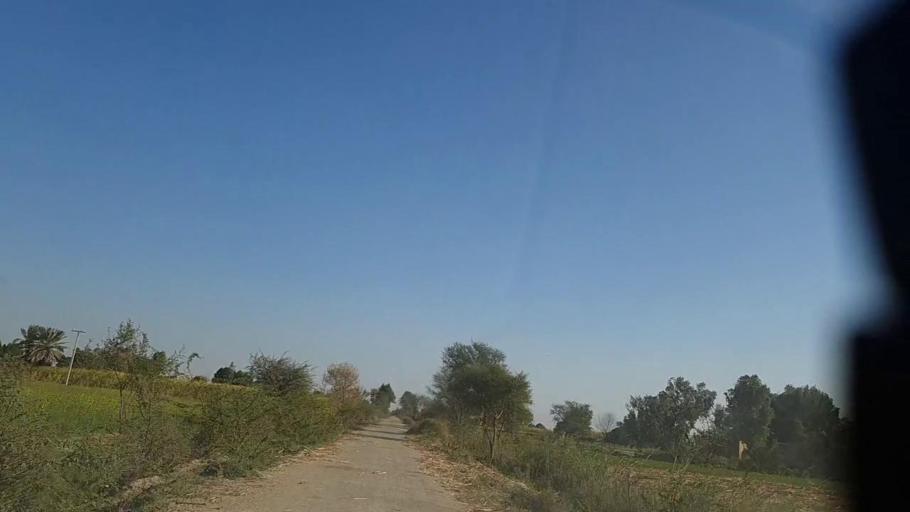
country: PK
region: Sindh
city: Digri
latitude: 25.1500
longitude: 69.0414
